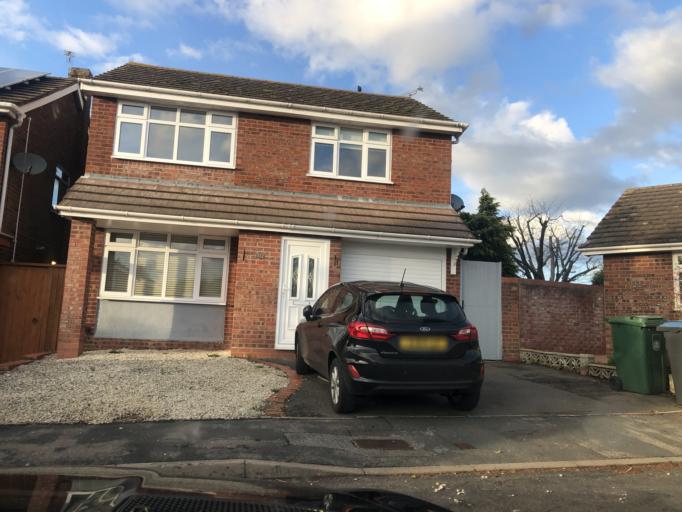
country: GB
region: England
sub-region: Warwickshire
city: Harbury
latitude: 52.2351
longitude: -1.4641
